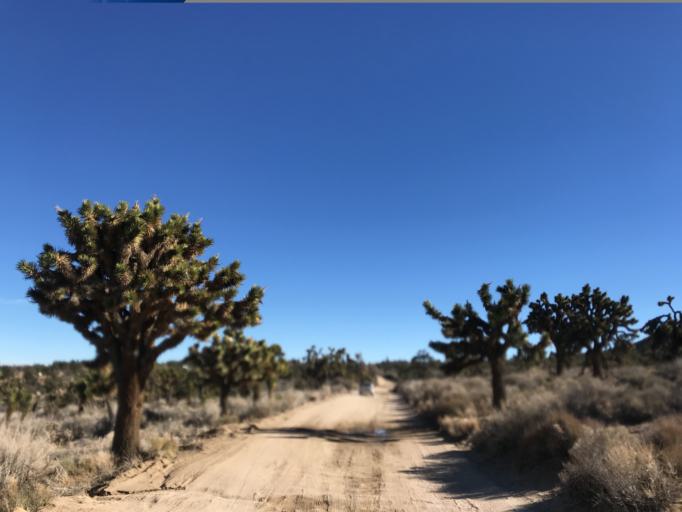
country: US
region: California
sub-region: San Bernardino County
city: Morongo Valley
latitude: 34.2175
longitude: -116.6174
